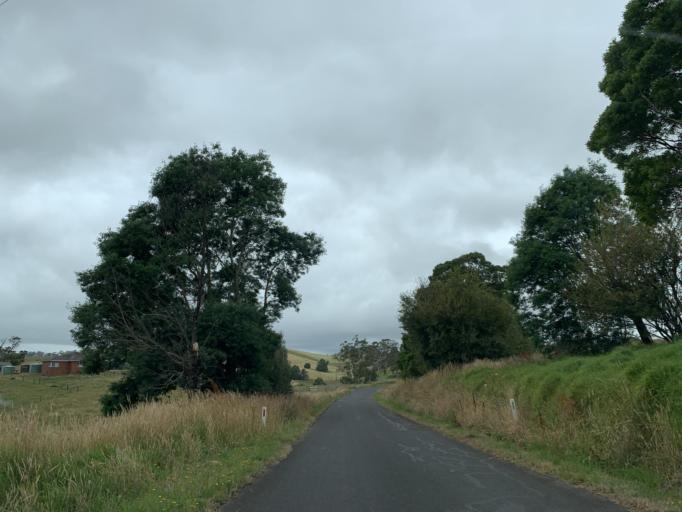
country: AU
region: Victoria
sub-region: Baw Baw
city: Warragul
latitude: -38.2940
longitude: 145.8563
